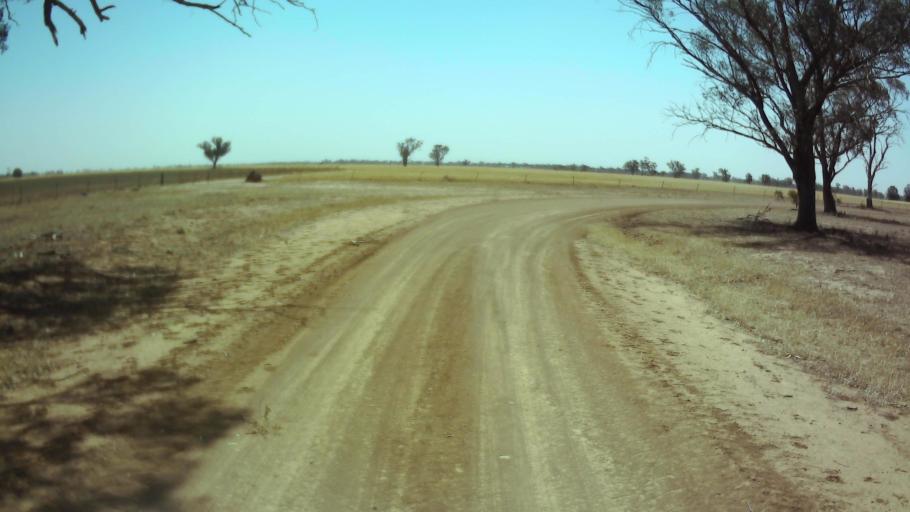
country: AU
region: New South Wales
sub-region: Weddin
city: Grenfell
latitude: -34.0020
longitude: 147.8768
